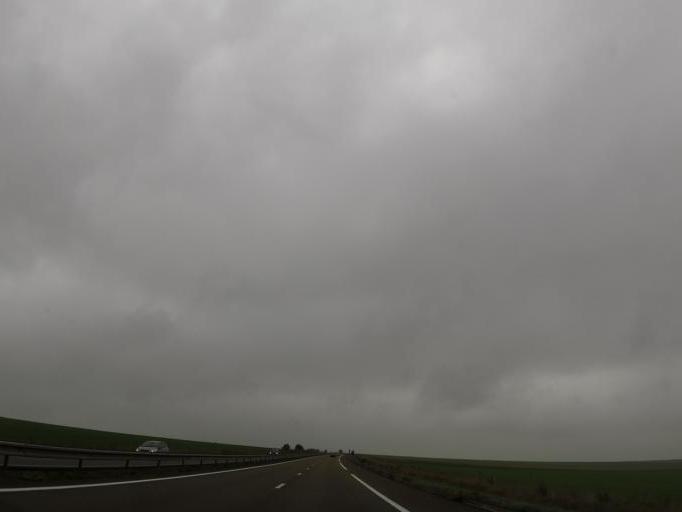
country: FR
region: Champagne-Ardenne
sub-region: Departement de la Marne
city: Mourmelon-le-Grand
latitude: 49.0853
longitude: 4.2608
